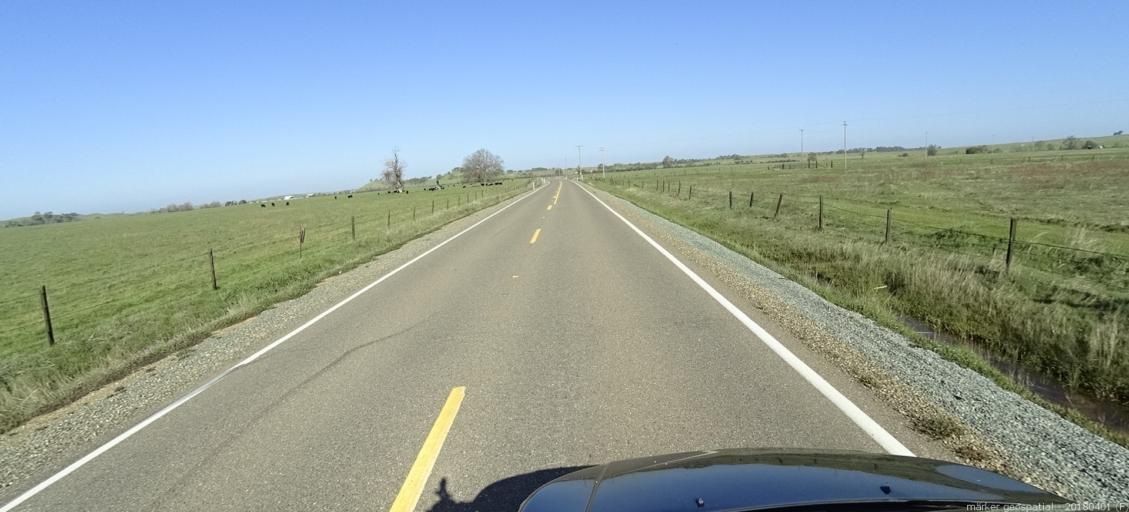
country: US
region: California
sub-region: Sacramento County
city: Rancho Murieta
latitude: 38.4193
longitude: -121.0429
